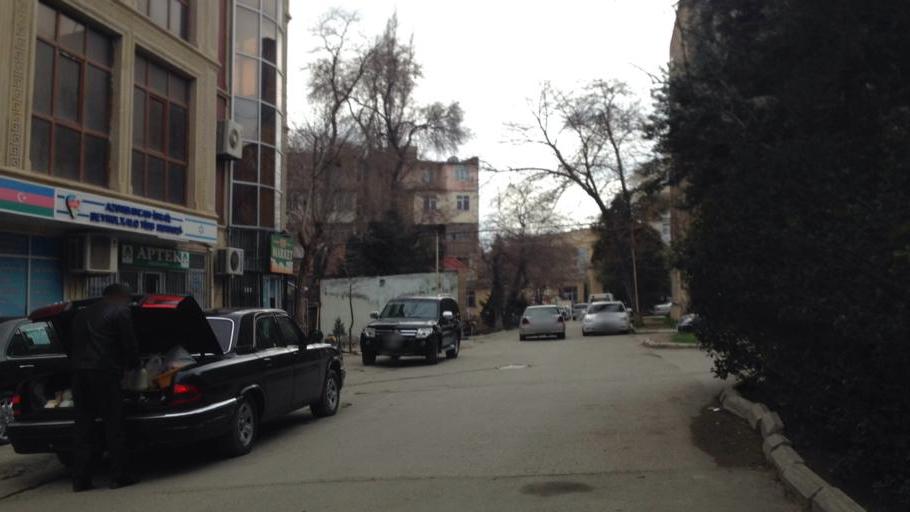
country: AZ
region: Baki
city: Bilajari
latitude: 40.4088
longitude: 49.8361
